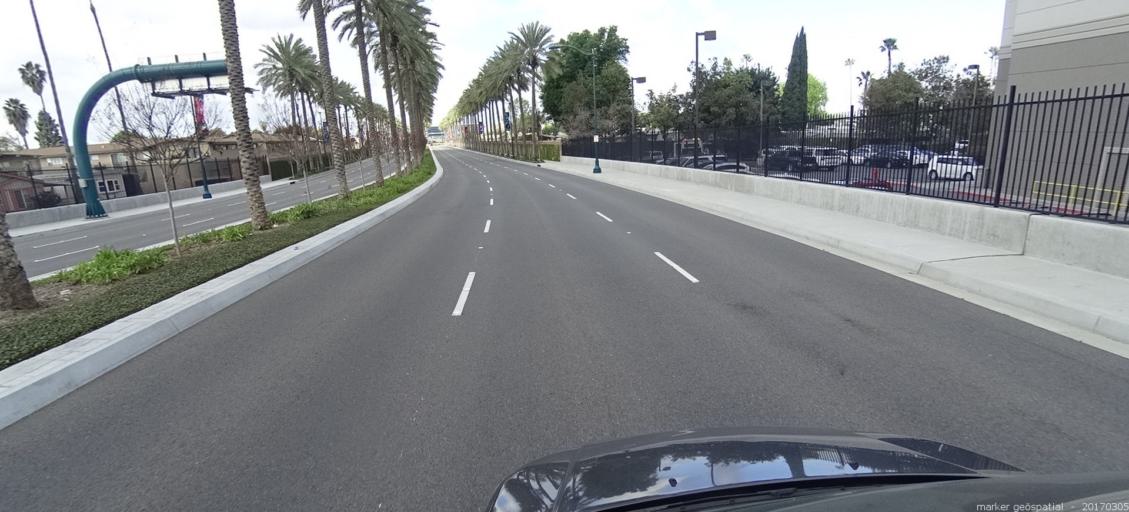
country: US
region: California
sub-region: Orange County
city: Anaheim
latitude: 33.8000
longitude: -117.9015
